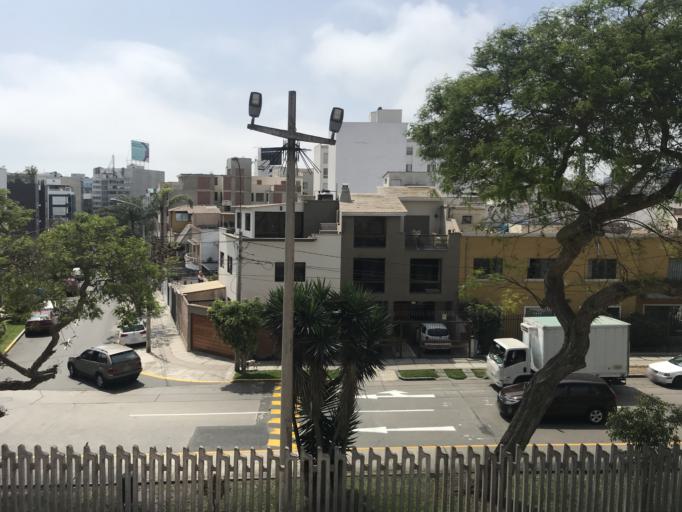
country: PE
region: Lima
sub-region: Lima
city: San Isidro
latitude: -12.1116
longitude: -77.0343
